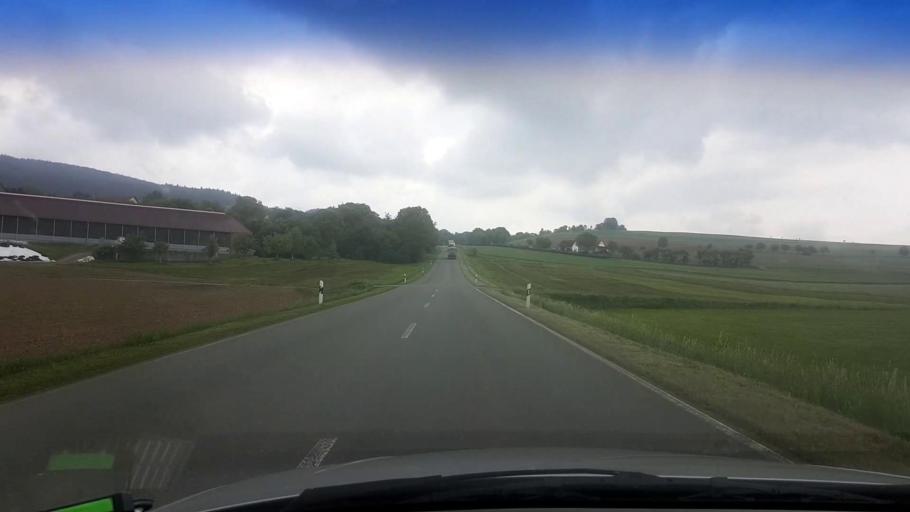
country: DE
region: Bavaria
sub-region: Upper Franconia
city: Reuth
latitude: 49.9941
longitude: 11.6804
